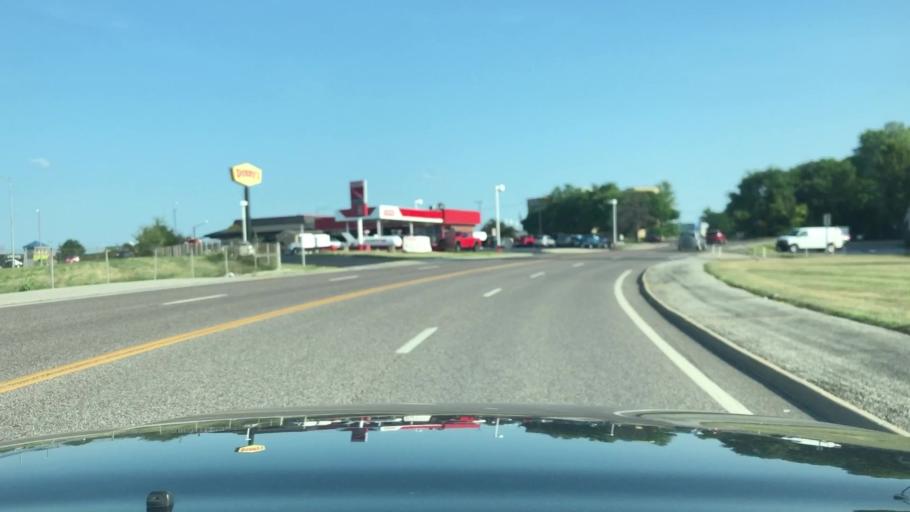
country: US
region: Missouri
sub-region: Saint Charles County
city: Saint Peters
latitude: 38.7936
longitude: -90.5673
